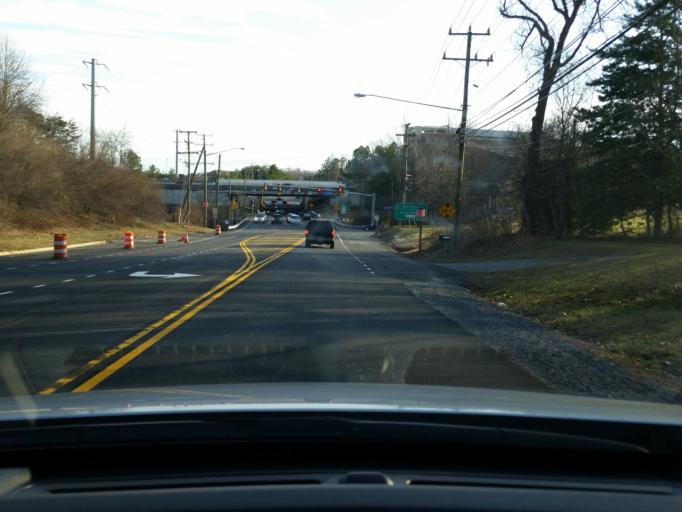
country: US
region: Virginia
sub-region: Fairfax County
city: Wolf Trap
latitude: 38.9501
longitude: -77.3118
